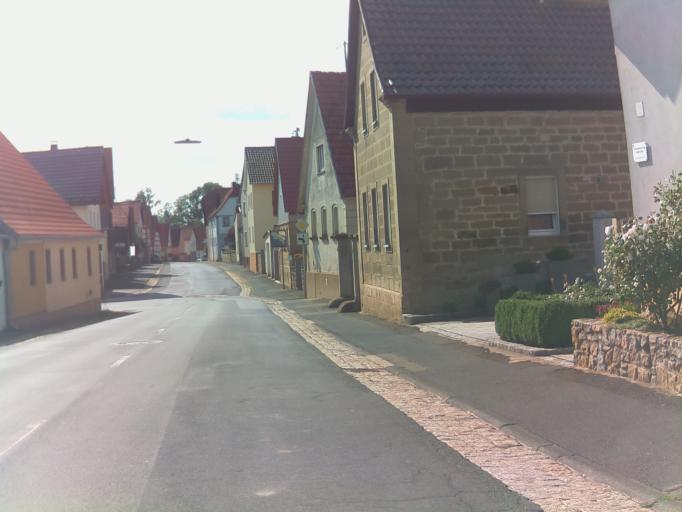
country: DE
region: Bavaria
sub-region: Regierungsbezirk Unterfranken
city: Bundorf
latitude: 50.2677
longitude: 10.5402
